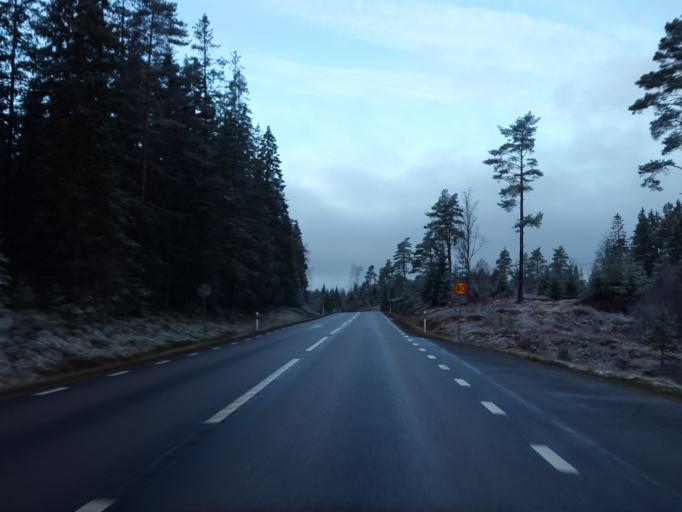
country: SE
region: Vaestra Goetaland
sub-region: Vargarda Kommun
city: Jonstorp
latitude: 57.8387
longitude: 12.6887
